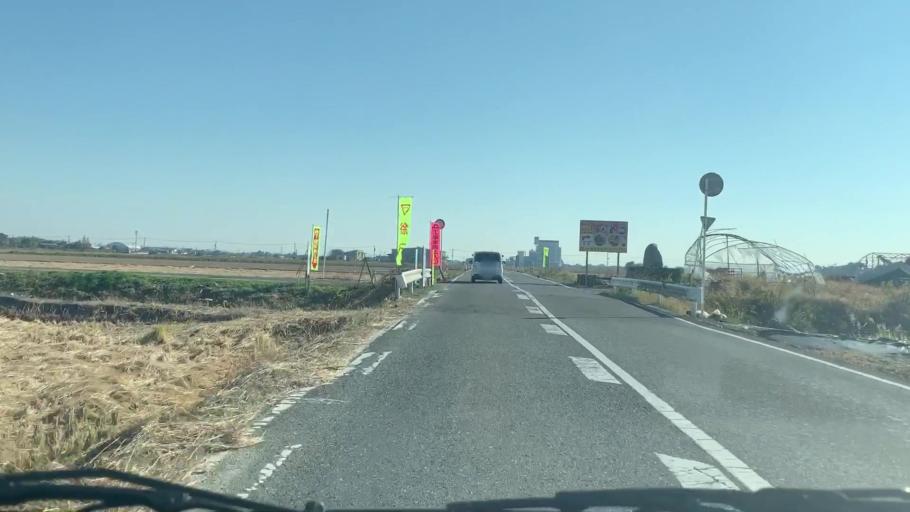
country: JP
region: Saga Prefecture
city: Saga-shi
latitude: 33.2276
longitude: 130.2788
